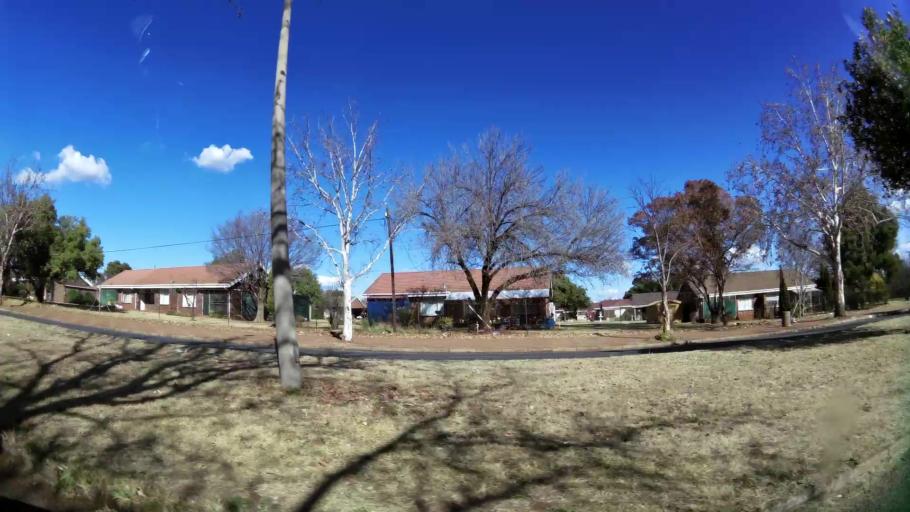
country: ZA
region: Gauteng
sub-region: West Rand District Municipality
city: Carletonville
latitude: -26.3582
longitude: 27.3866
